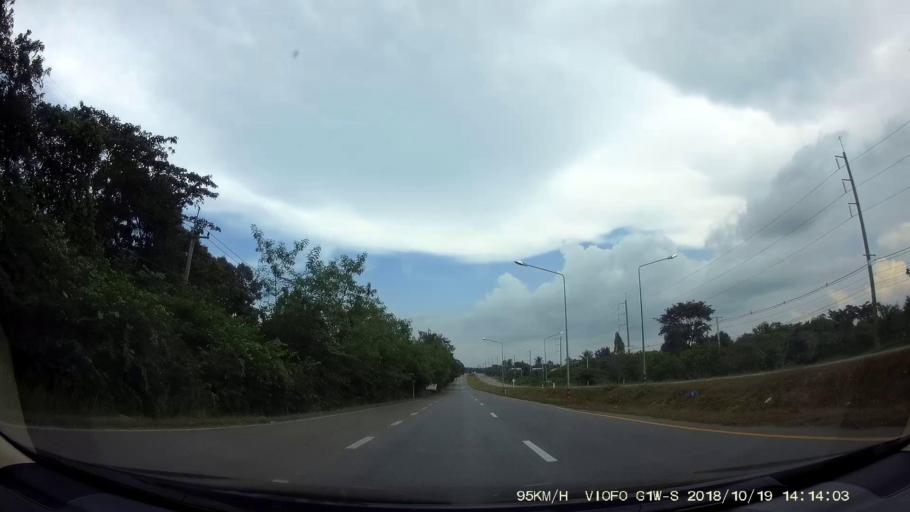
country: TH
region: Chaiyaphum
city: Khon Sawan
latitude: 15.9676
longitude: 102.1843
